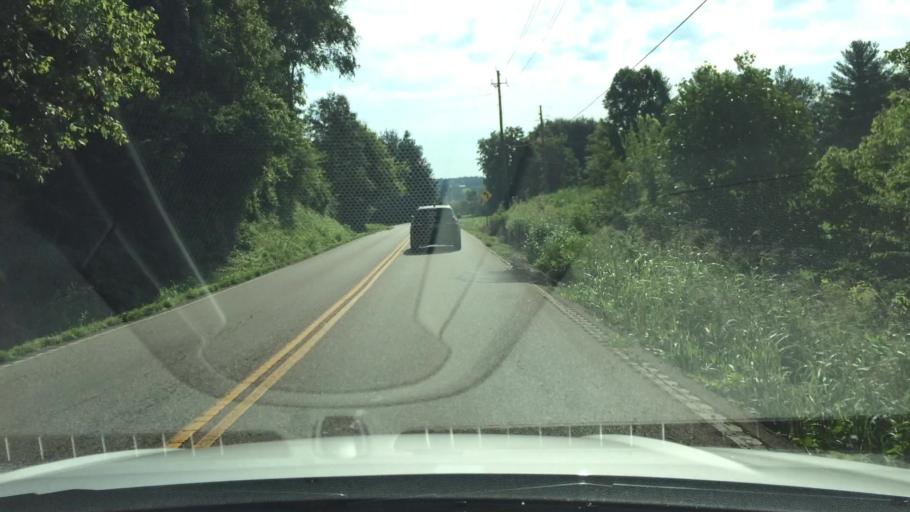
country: US
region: Tennessee
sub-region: Sevier County
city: Sevierville
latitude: 35.9233
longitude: -83.5921
